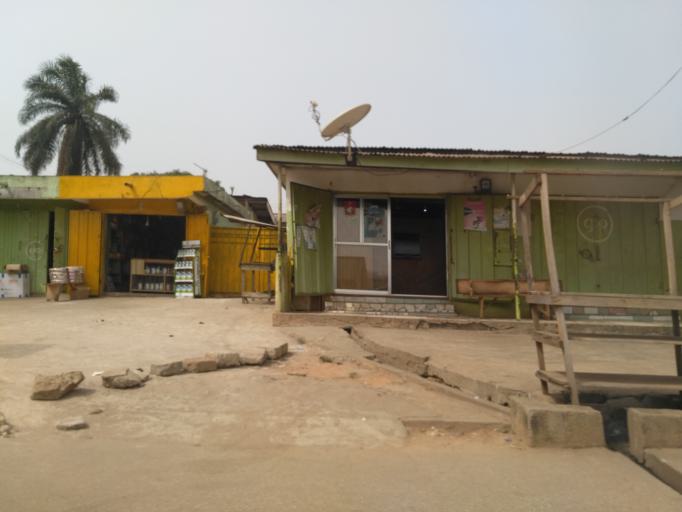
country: GH
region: Ashanti
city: Kumasi
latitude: 6.7007
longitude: -1.6032
